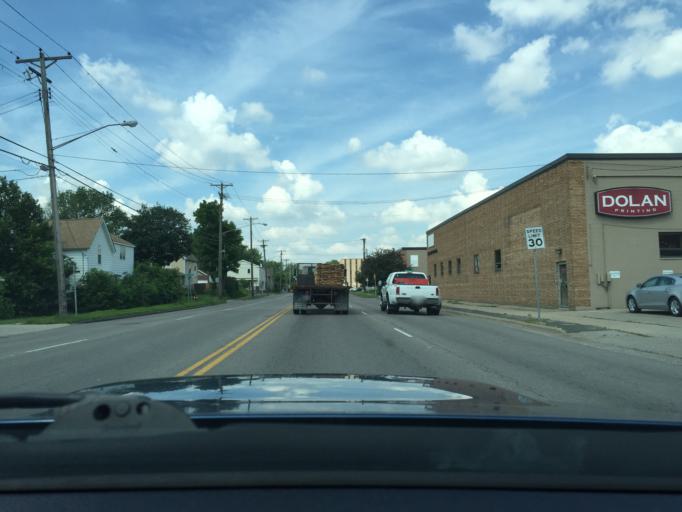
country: US
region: Minnesota
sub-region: Ramsey County
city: Lauderdale
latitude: 44.9915
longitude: -93.2192
